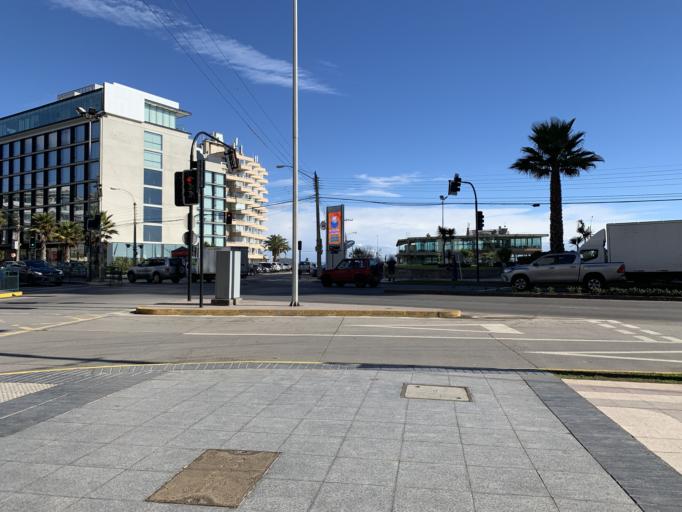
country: CL
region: Valparaiso
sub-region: Provincia de Valparaiso
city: Vina del Mar
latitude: -33.0145
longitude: -71.5548
